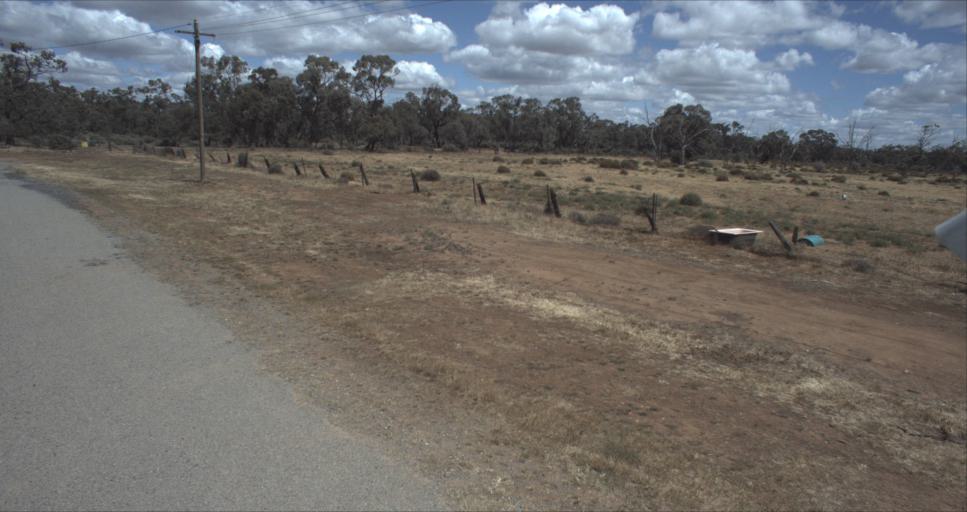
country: AU
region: New South Wales
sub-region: Murrumbidgee Shire
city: Darlington Point
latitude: -34.5212
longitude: 146.1829
